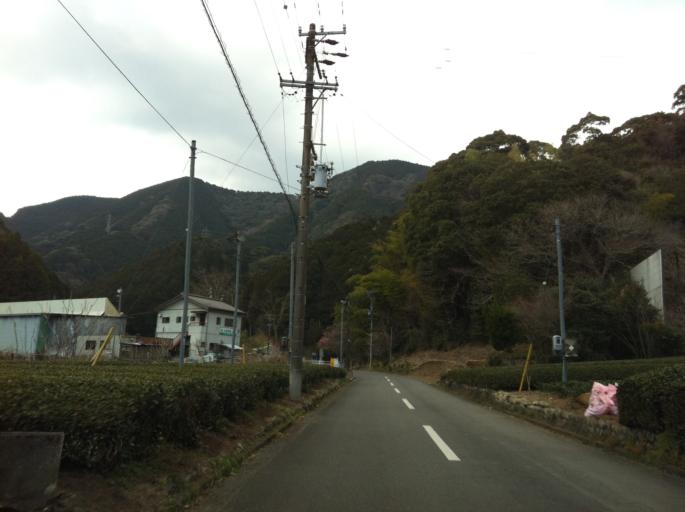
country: JP
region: Shizuoka
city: Shizuoka-shi
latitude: 35.0319
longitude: 138.3337
